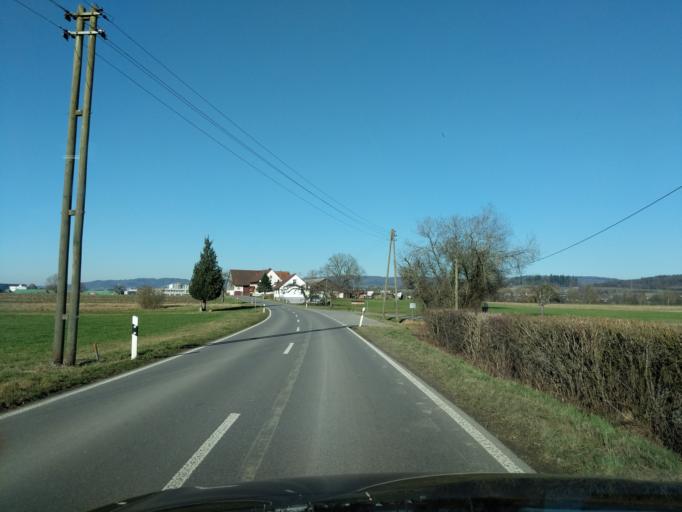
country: DE
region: Baden-Wuerttemberg
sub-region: Tuebingen Region
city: Salem
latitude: 47.7482
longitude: 9.3051
